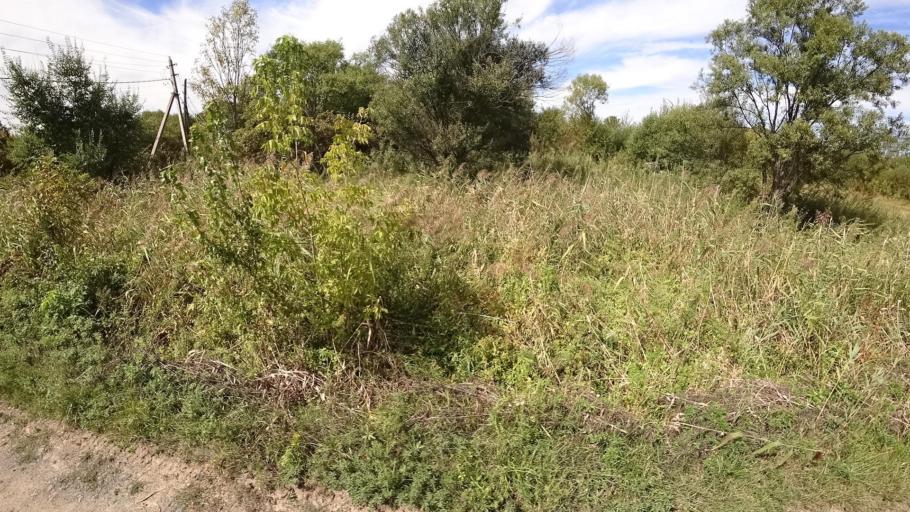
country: RU
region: Primorskiy
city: Yakovlevka
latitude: 44.6399
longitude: 133.6006
